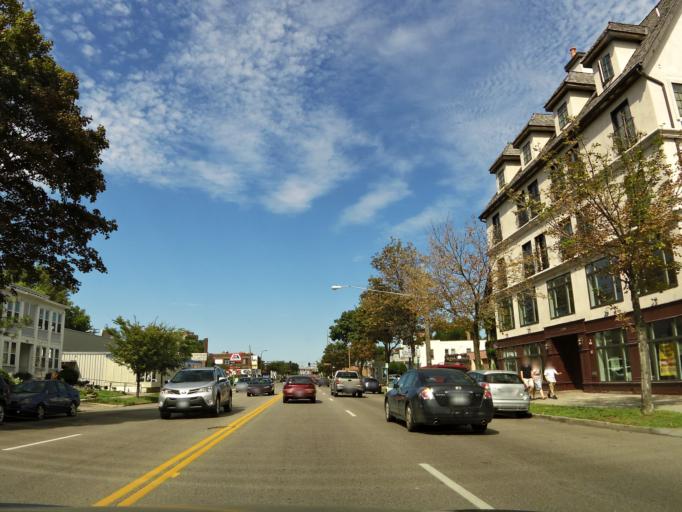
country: US
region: Minnesota
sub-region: Hennepin County
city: Minneapolis
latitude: 44.9596
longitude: -93.2881
